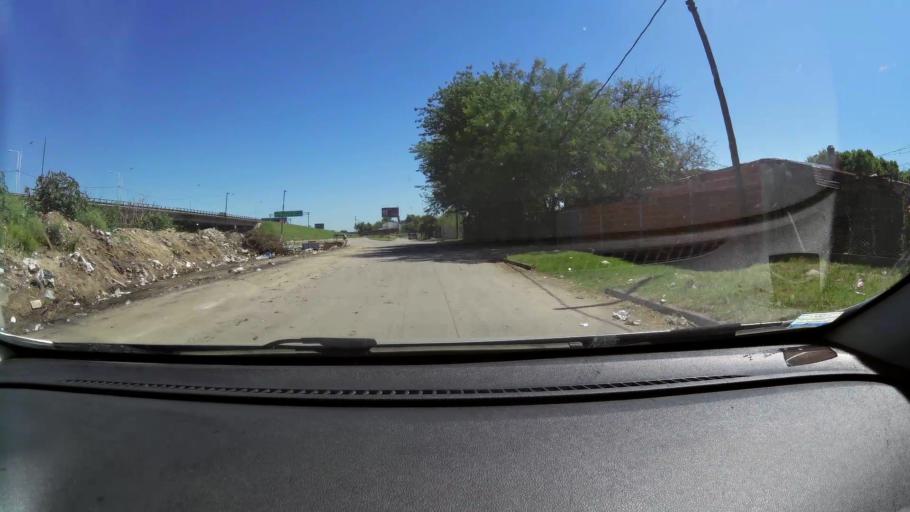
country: AR
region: Santa Fe
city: Perez
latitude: -32.9541
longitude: -60.7210
